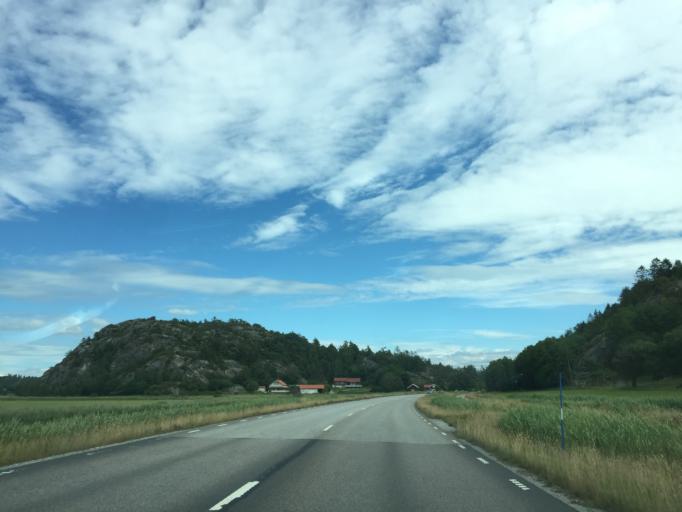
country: SE
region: Vaestra Goetaland
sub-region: Tjorns Kommun
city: Skaerhamn
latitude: 58.0230
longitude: 11.6383
